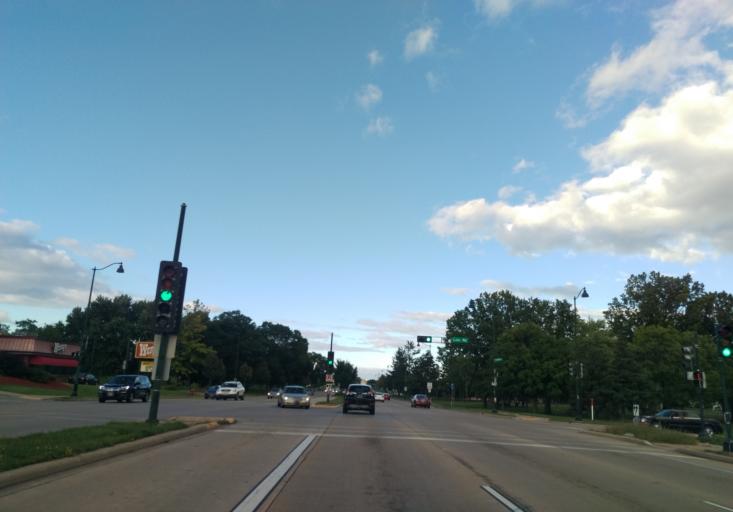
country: US
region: Wisconsin
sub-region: Dane County
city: Monona
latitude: 43.1211
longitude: -89.3183
